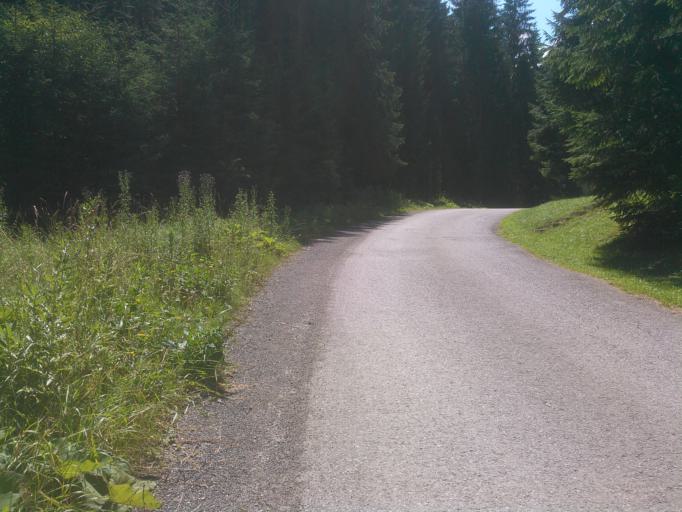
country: SK
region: Zilinsky
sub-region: Okres Liptovsky Mikulas
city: Liptovsky Mikulas
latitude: 48.9852
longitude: 19.5056
